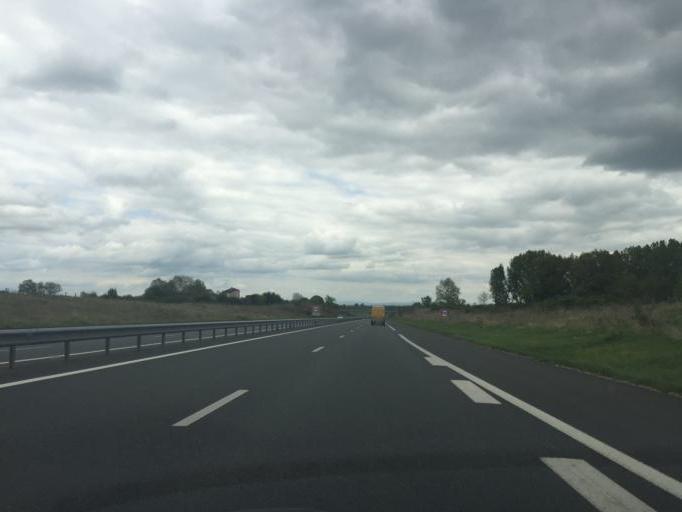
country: FR
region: Rhone-Alpes
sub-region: Departement de la Loire
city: La Pacaudiere
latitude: 46.1869
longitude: 3.8665
